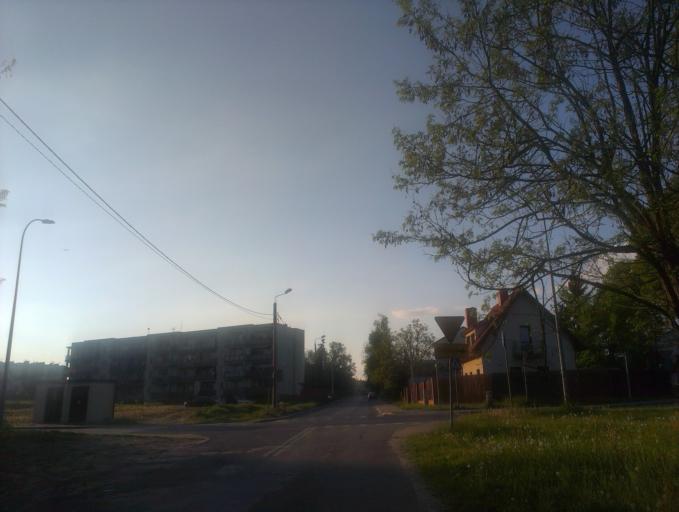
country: PL
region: Masovian Voivodeship
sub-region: Powiat piaseczynski
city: Zabieniec
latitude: 52.0613
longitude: 21.0316
